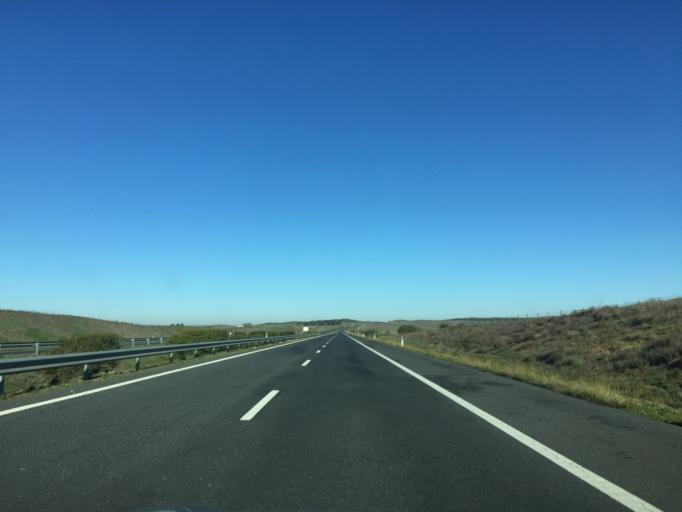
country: PT
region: Beja
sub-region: Aljustrel
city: Aljustrel
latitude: 37.7867
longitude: -8.2180
